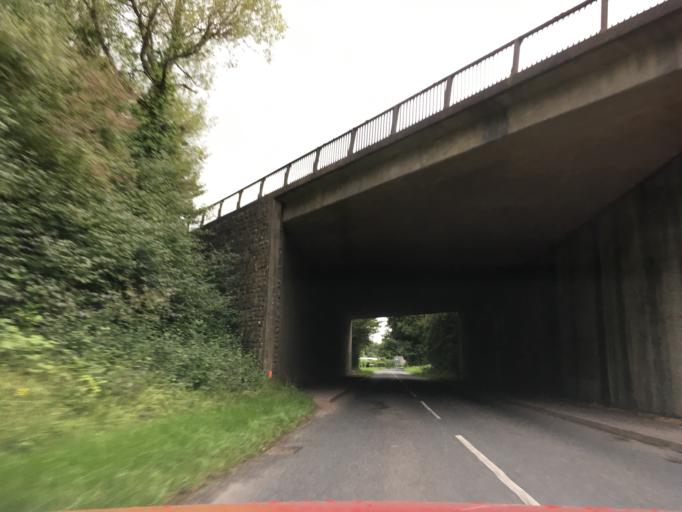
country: GB
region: Wales
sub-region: Monmouthshire
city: Llangybi
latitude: 51.6712
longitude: -2.8772
